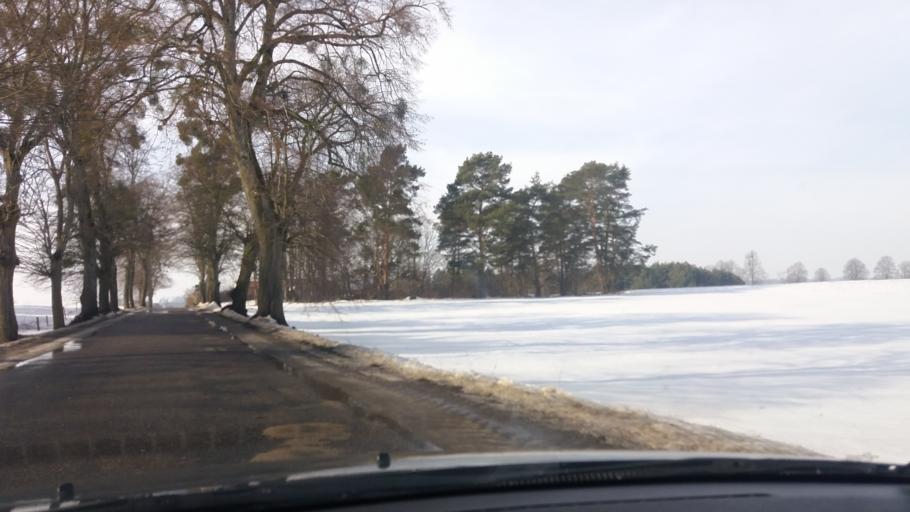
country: PL
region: Warmian-Masurian Voivodeship
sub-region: Powiat lidzbarski
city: Lidzbark Warminski
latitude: 54.1048
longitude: 20.7011
